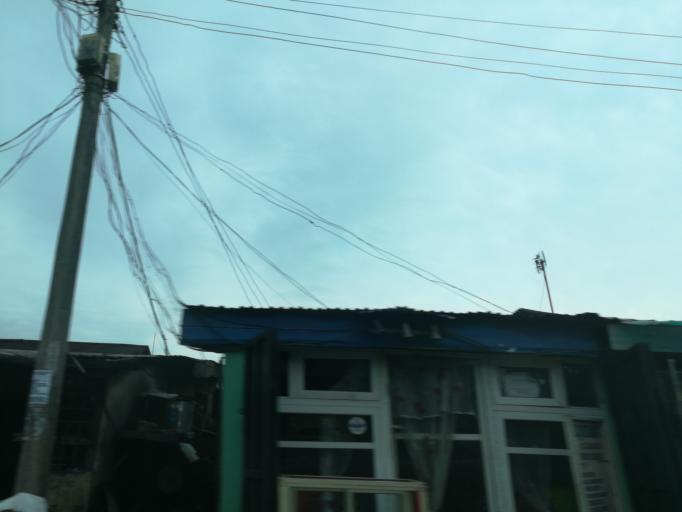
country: NG
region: Rivers
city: Port Harcourt
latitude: 4.8352
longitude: 7.0234
